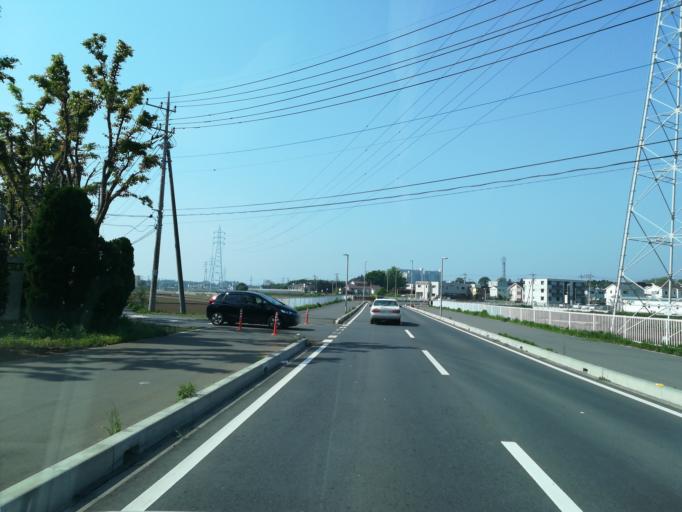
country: JP
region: Ibaraki
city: Naka
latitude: 36.0944
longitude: 140.0948
